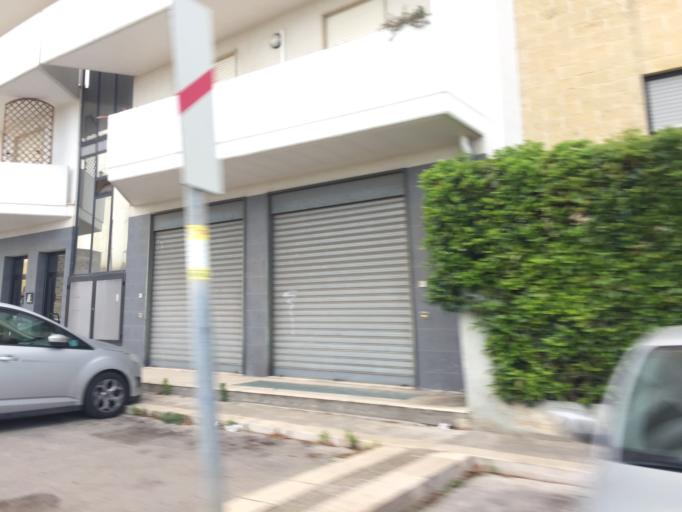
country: IT
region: Apulia
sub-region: Provincia di Bari
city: Capurso
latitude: 41.0510
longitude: 16.9218
